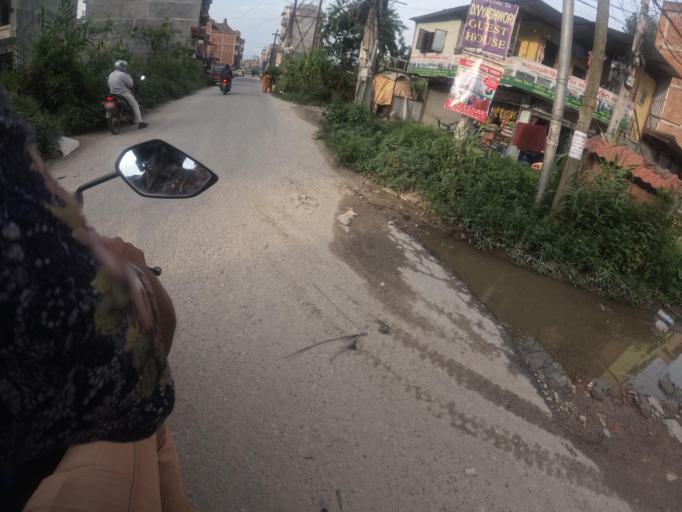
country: NP
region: Central Region
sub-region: Bagmati Zone
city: Bhaktapur
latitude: 27.6748
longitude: 85.3877
